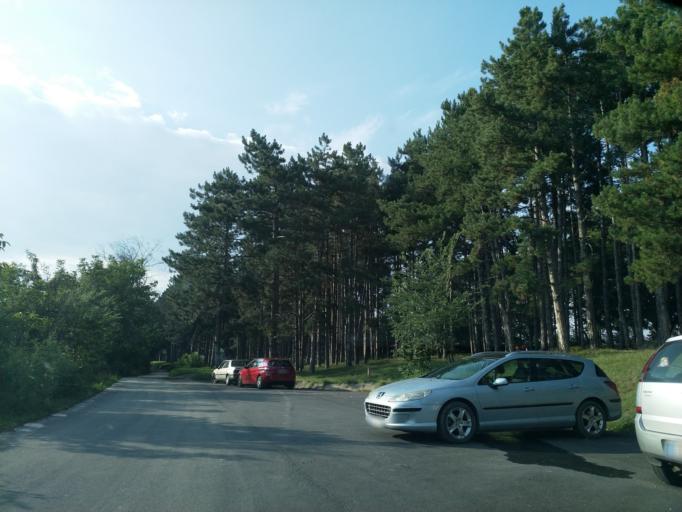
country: RS
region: Central Serbia
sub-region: Pomoravski Okrug
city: Jagodina
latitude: 43.9771
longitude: 21.2463
